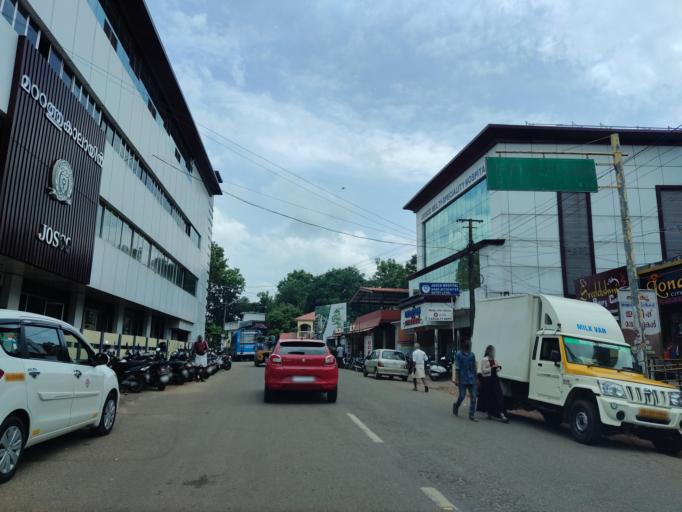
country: IN
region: Kerala
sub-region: Alappuzha
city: Mavelikara
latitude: 9.2289
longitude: 76.6270
